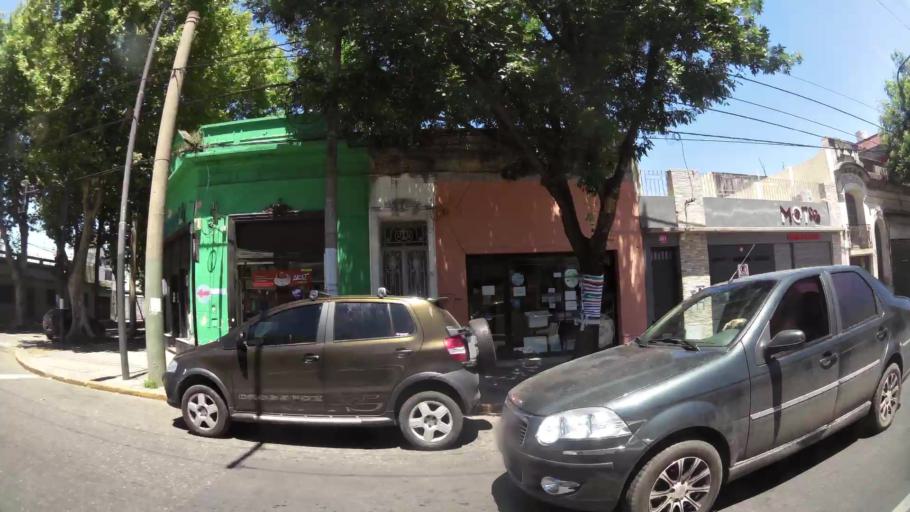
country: AR
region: Santa Fe
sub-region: Departamento de Rosario
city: Rosario
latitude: -32.9423
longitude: -60.6914
